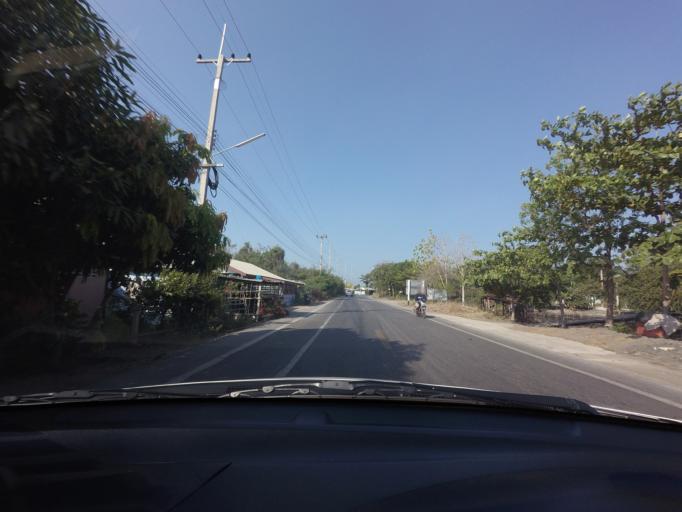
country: TH
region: Samut Sakhon
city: Ban Phaeo
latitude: 13.5113
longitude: 100.1209
